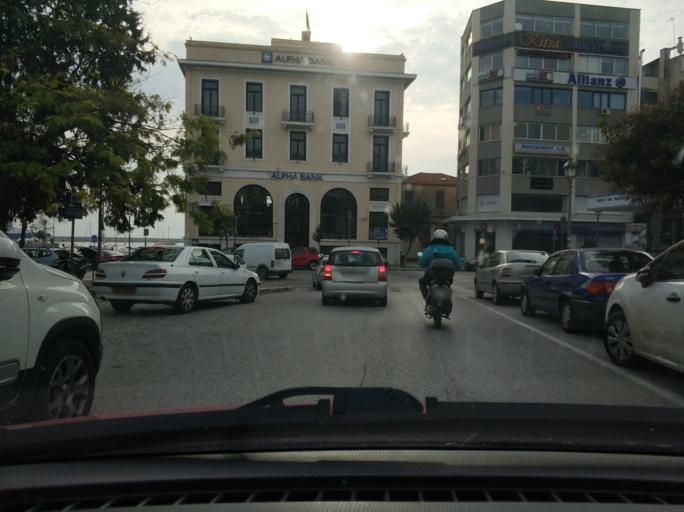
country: GR
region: East Macedonia and Thrace
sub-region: Nomos Kavalas
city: Kavala
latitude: 40.9369
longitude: 24.4116
